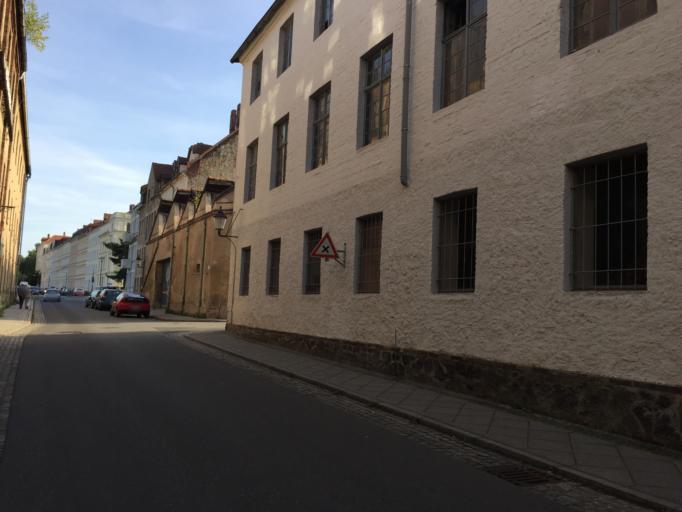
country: DE
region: Saxony
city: Goerlitz
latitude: 51.1555
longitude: 14.9956
